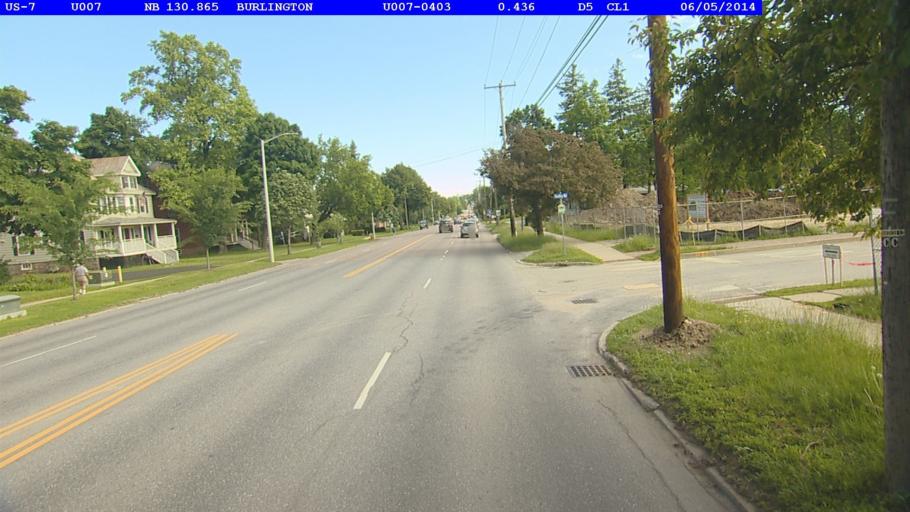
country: US
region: Vermont
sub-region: Chittenden County
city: Burlington
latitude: 44.4521
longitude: -73.2088
